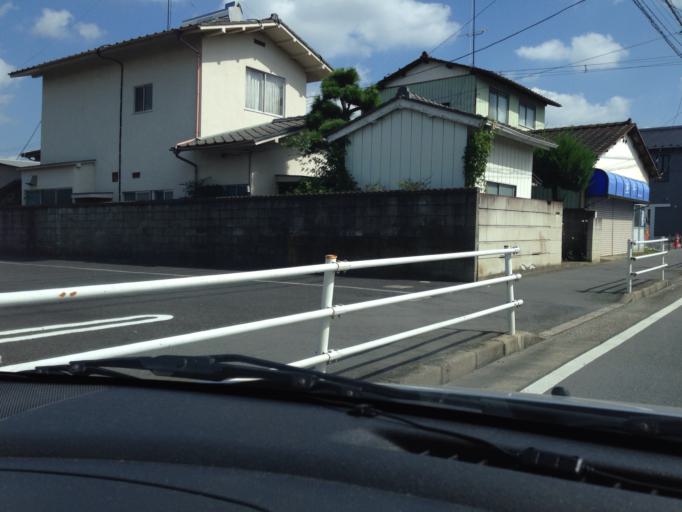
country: JP
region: Ibaraki
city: Mito-shi
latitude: 36.4010
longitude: 140.4384
